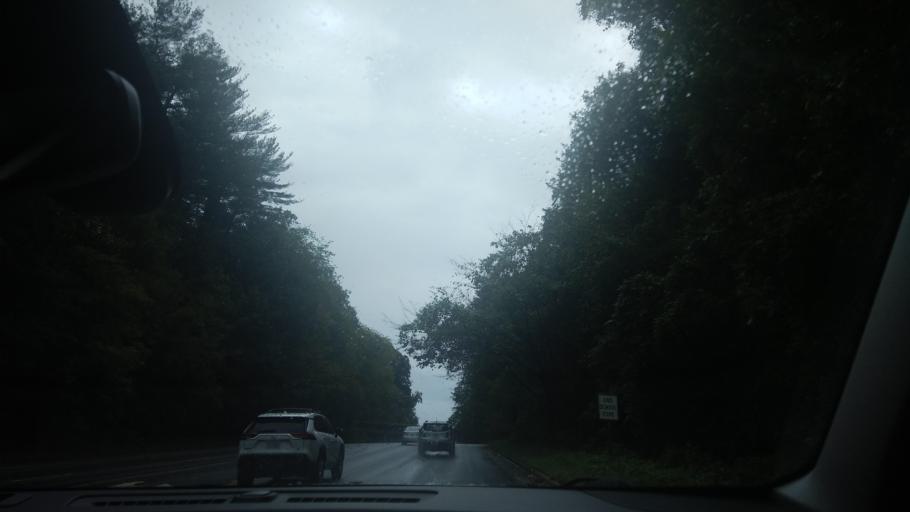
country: US
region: North Carolina
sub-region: Buncombe County
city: Biltmore Forest
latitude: 35.5210
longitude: -82.5292
